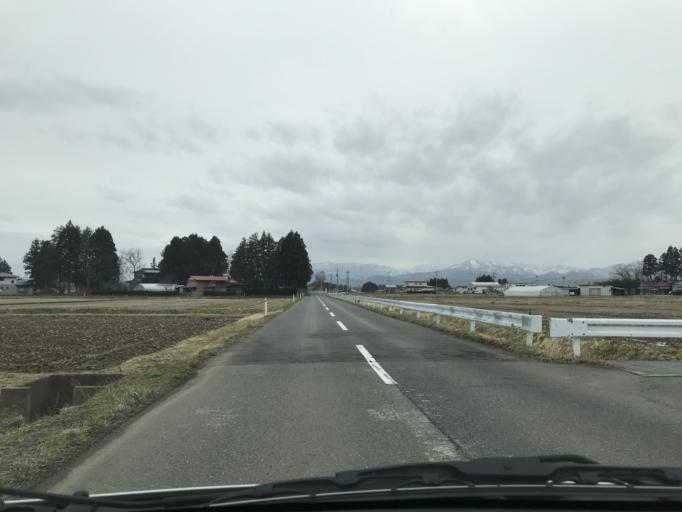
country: JP
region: Iwate
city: Kitakami
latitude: 39.3155
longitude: 141.0629
